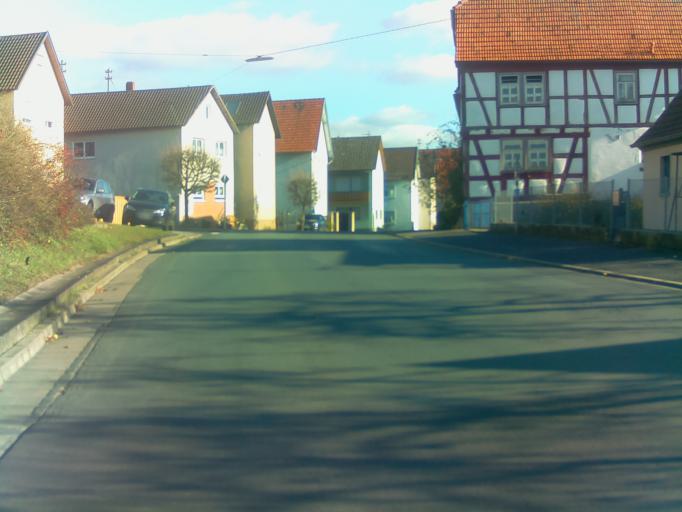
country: DE
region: Bavaria
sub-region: Regierungsbezirk Unterfranken
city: Herbstadt
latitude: 50.3109
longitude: 10.5240
